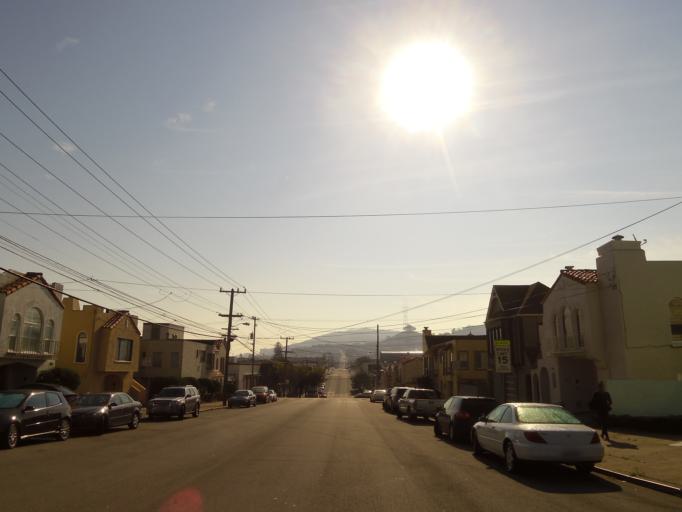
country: US
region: California
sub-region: San Mateo County
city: Daly City
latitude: 37.7573
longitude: -122.4899
